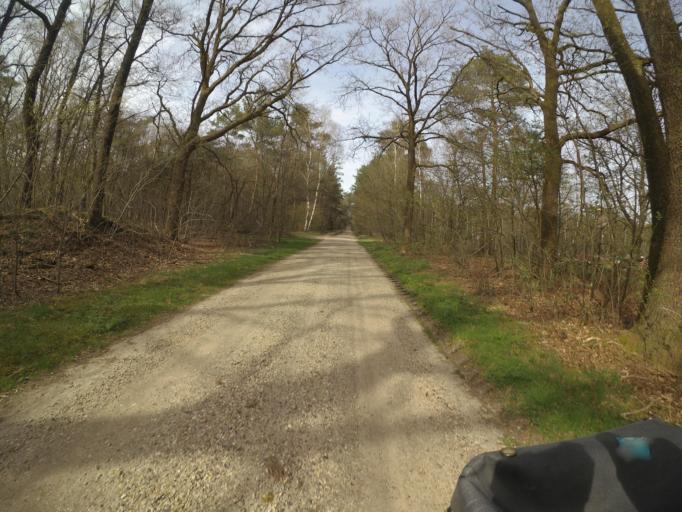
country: NL
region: Gelderland
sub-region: Gemeente Barneveld
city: Garderen
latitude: 52.2224
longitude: 5.7486
